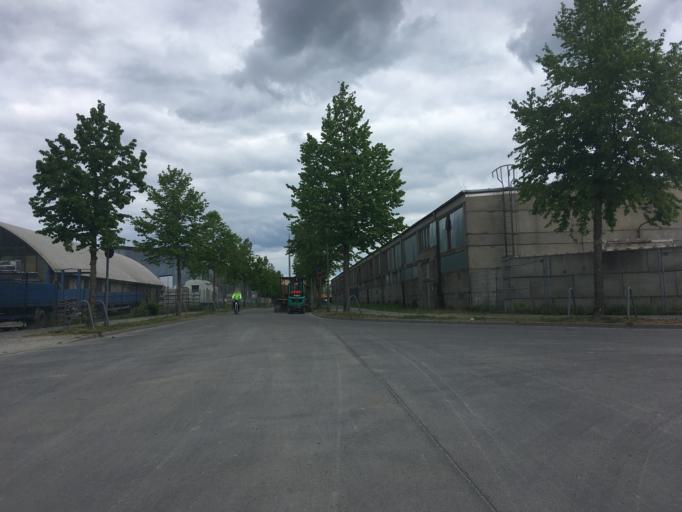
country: DE
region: Berlin
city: Neu-Hohenschoenhausen
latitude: 52.5538
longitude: 13.5288
